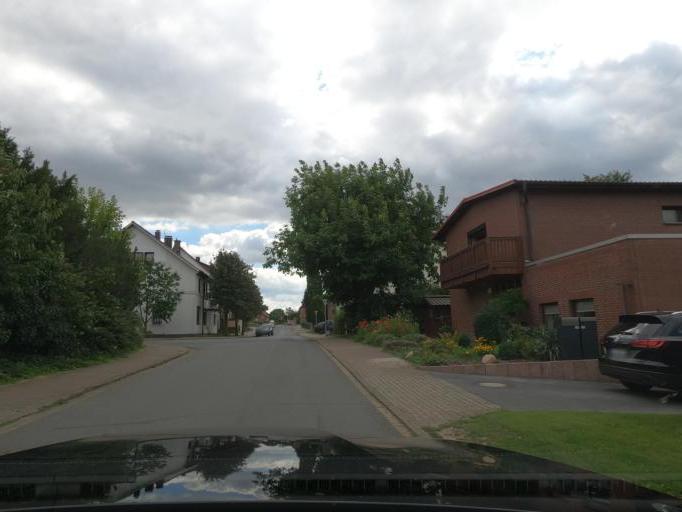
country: DE
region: Lower Saxony
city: Hohenhameln
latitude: 52.2606
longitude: 10.0621
